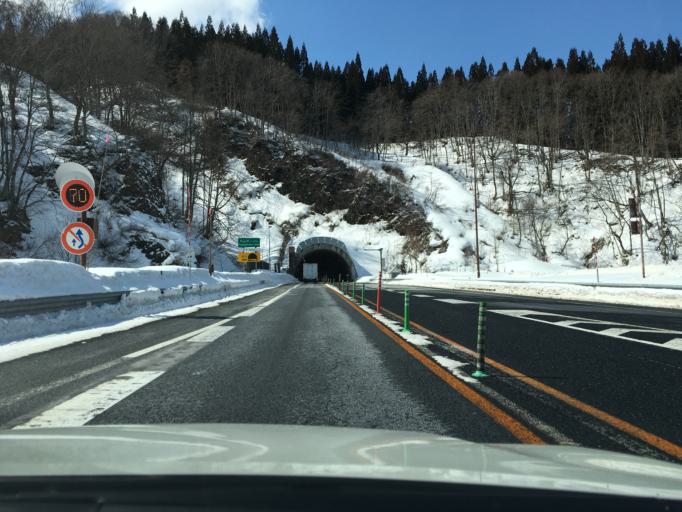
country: JP
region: Yamagata
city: Sagae
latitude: 38.4453
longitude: 140.0079
